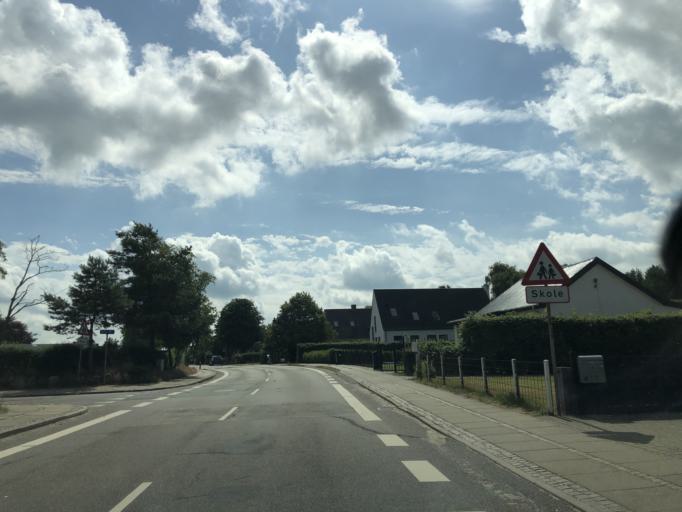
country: DK
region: Central Jutland
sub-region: Ikast-Brande Kommune
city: Brande
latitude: 55.9426
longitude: 9.1356
